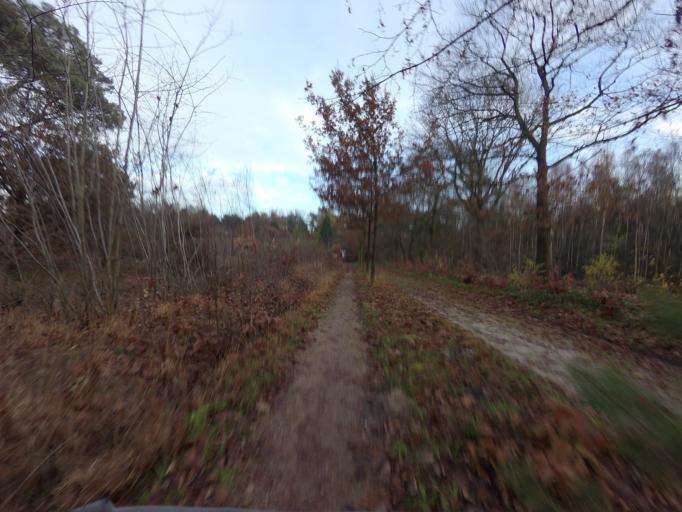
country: NL
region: North Brabant
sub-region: Gemeente Breda
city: Breda
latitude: 51.5086
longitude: 4.8108
